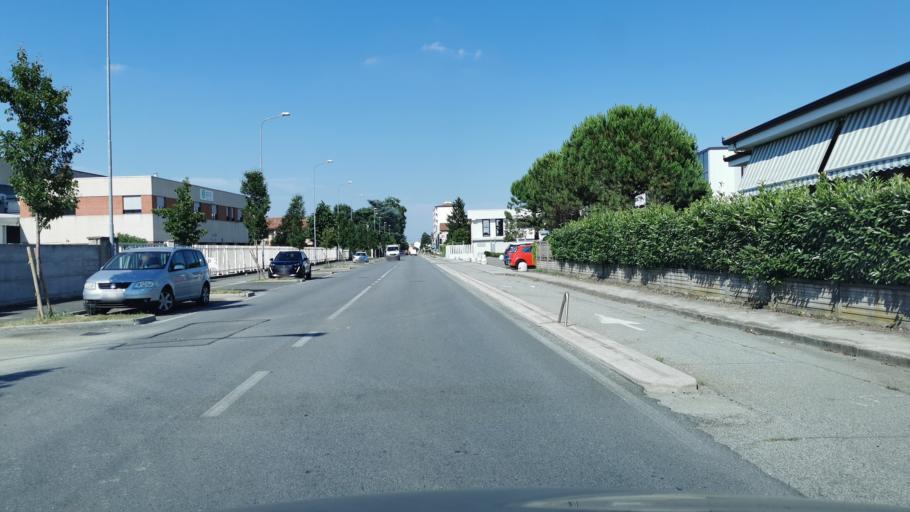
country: IT
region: Piedmont
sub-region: Provincia di Torino
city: Brandizzo
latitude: 45.1714
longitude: 7.8275
